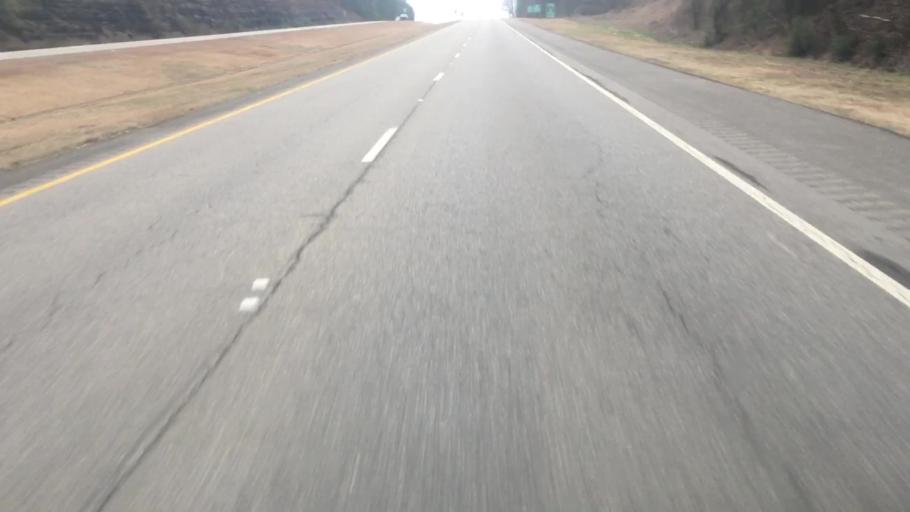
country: US
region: Alabama
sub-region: Walker County
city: Sumiton
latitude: 33.7681
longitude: -87.0712
